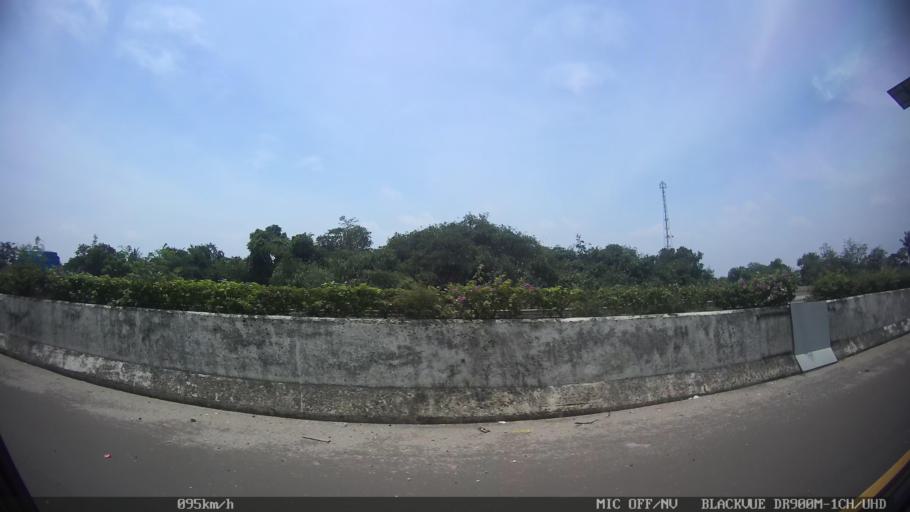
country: ID
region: West Java
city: Kresek
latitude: -6.1800
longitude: 106.3910
